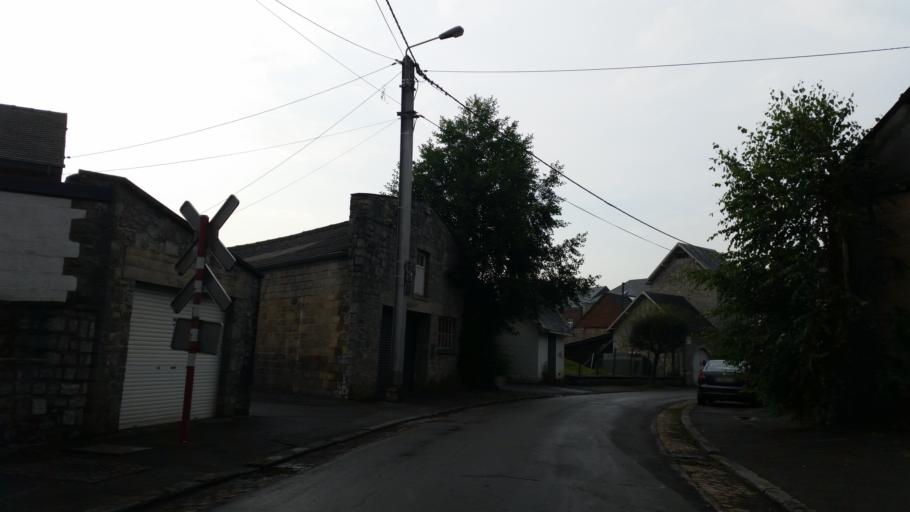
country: BE
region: Wallonia
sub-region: Province de Namur
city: Rochefort
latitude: 50.1252
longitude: 5.1859
